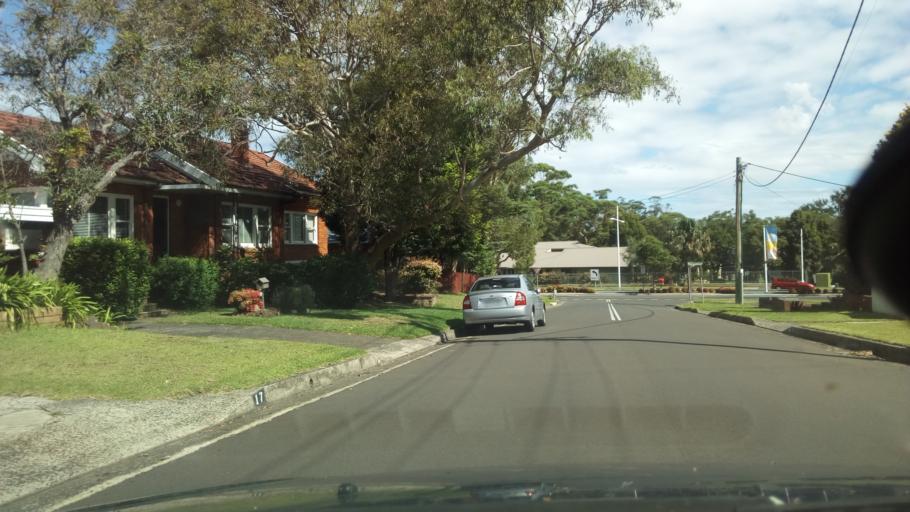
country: AU
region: New South Wales
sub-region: Wollongong
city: Fairy Meadow
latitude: -34.4019
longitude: 150.8880
